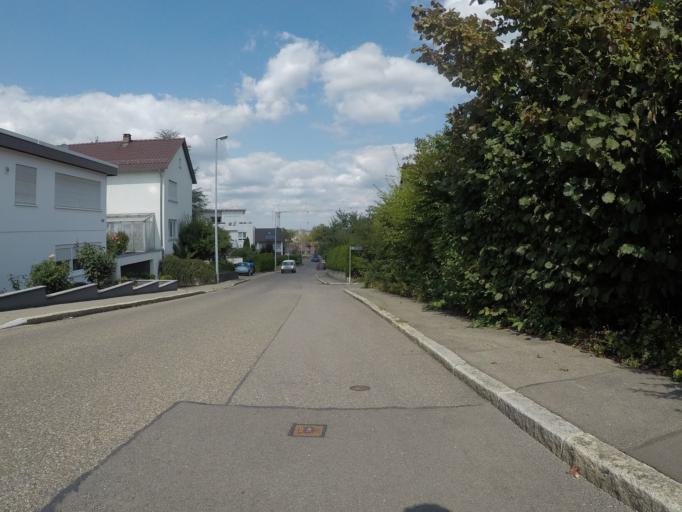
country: DE
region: Baden-Wuerttemberg
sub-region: Tuebingen Region
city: Reutlingen
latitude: 48.4776
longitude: 9.2120
